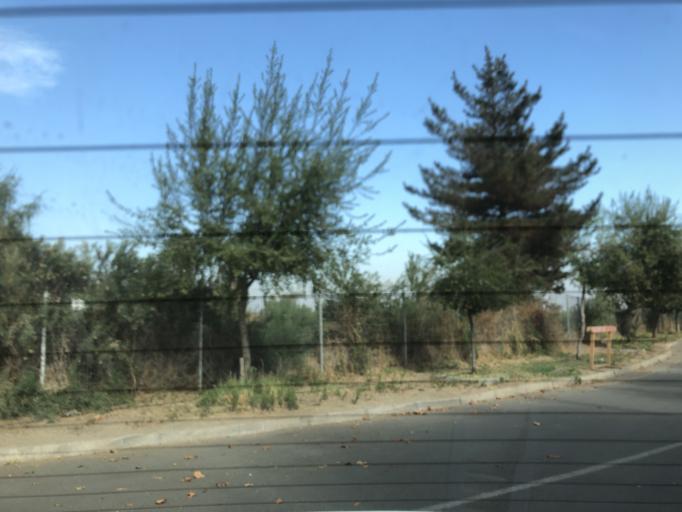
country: CL
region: Santiago Metropolitan
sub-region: Provincia de Cordillera
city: Puente Alto
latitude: -33.5781
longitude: -70.5423
